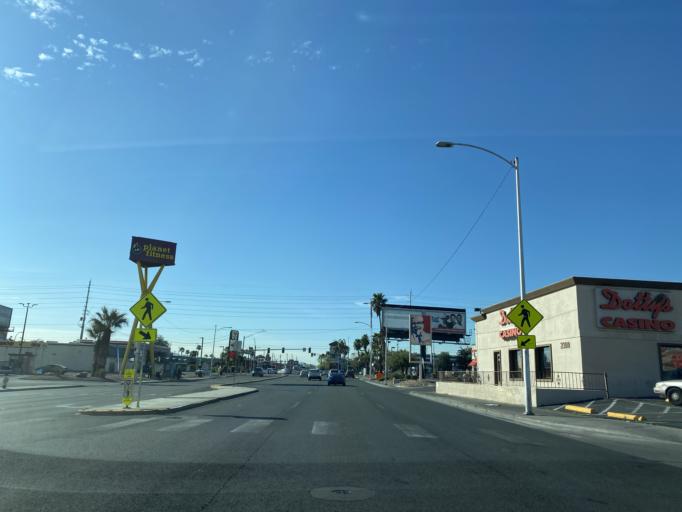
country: US
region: Nevada
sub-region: Clark County
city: Winchester
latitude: 36.1457
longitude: -115.1371
